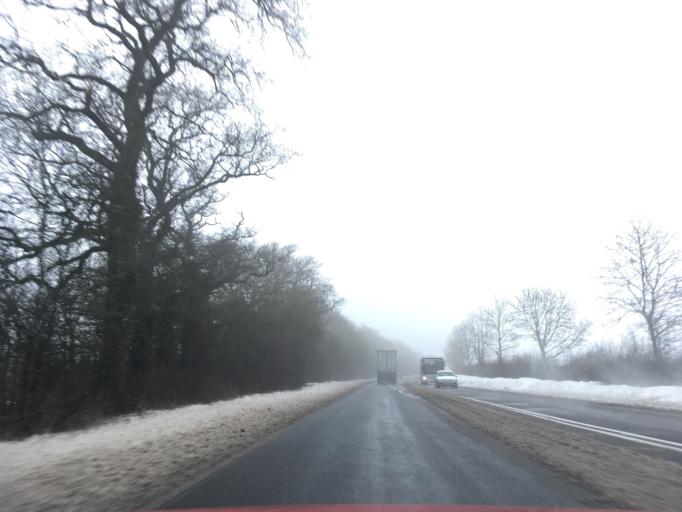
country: GB
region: England
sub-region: Warwickshire
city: Stratford-upon-Avon
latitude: 52.2211
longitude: -1.7081
